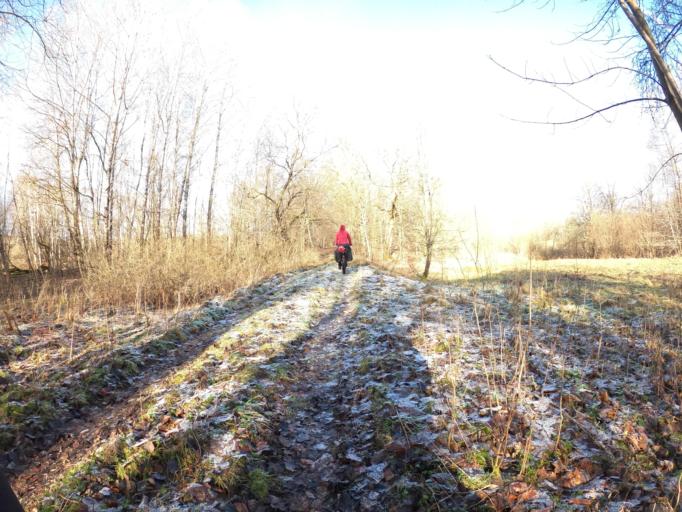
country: PL
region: West Pomeranian Voivodeship
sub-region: Powiat koszalinski
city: Polanow
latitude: 54.1352
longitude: 16.7726
